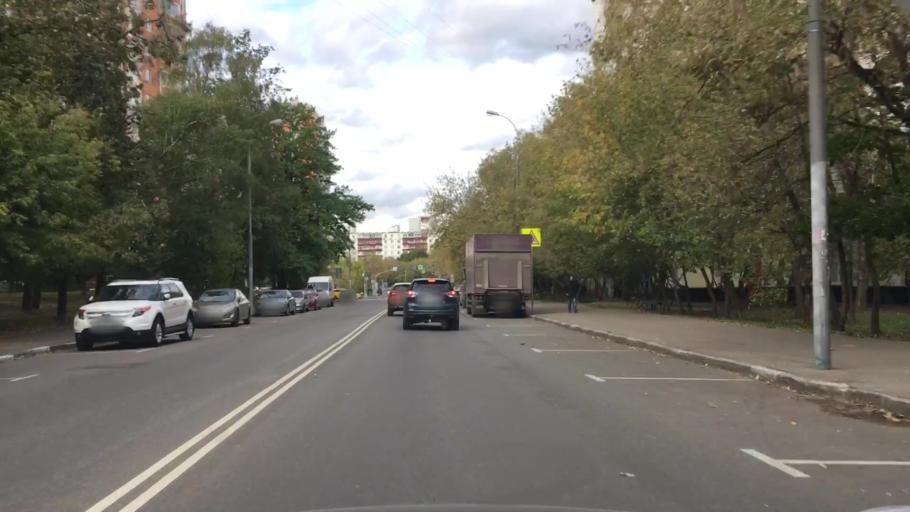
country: RU
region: Moscow
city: Gol'yanovo
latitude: 55.8081
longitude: 37.8179
